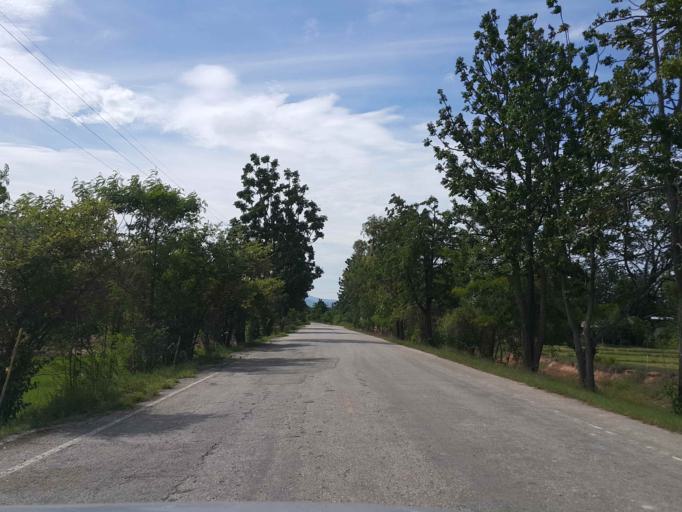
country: TH
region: Sukhothai
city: Ban Dan Lan Hoi
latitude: 17.1256
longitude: 99.5306
